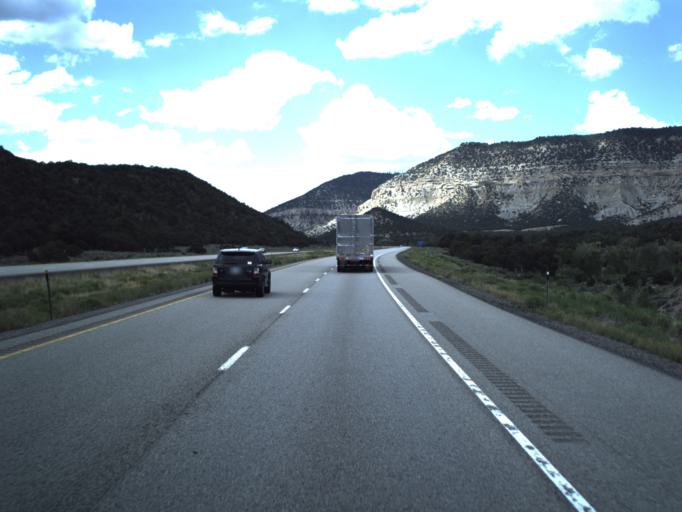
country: US
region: Utah
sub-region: Emery County
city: Ferron
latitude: 38.7560
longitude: -111.3975
